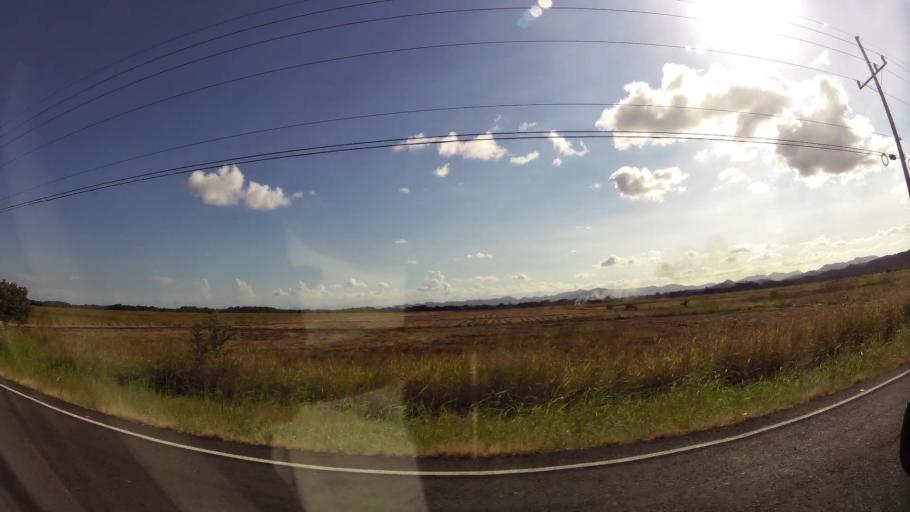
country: CR
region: Guanacaste
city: Sardinal
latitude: 10.5660
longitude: -85.6118
